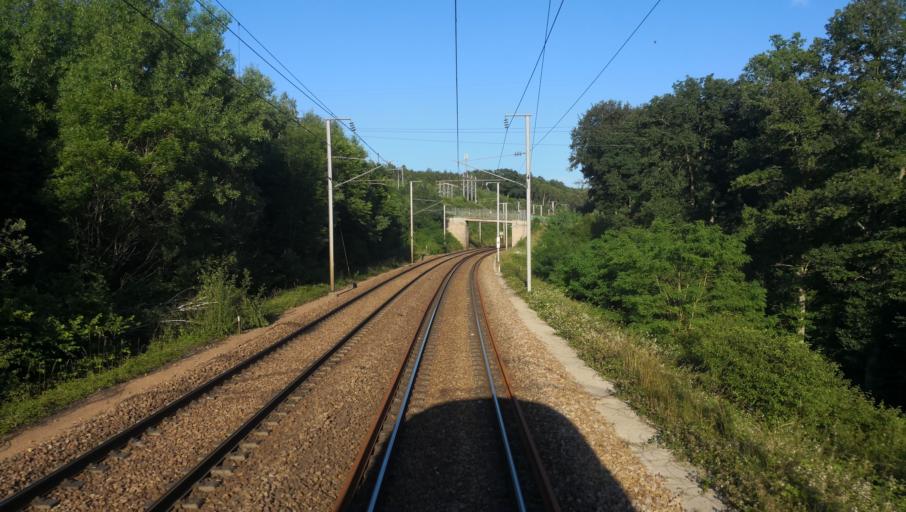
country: FR
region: Haute-Normandie
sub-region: Departement de l'Eure
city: Beaumont-le-Roger
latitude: 49.0333
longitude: 0.8126
